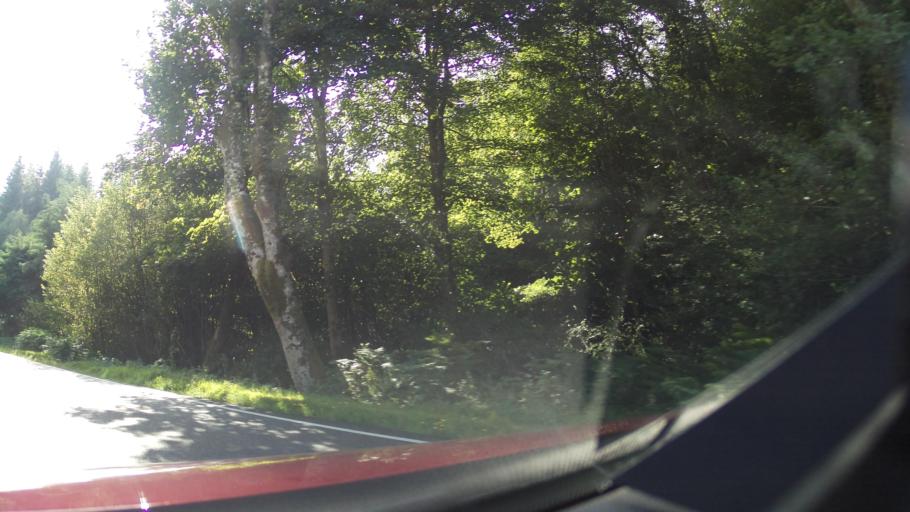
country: GB
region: Scotland
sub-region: Highland
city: Beauly
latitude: 57.1905
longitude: -4.6186
